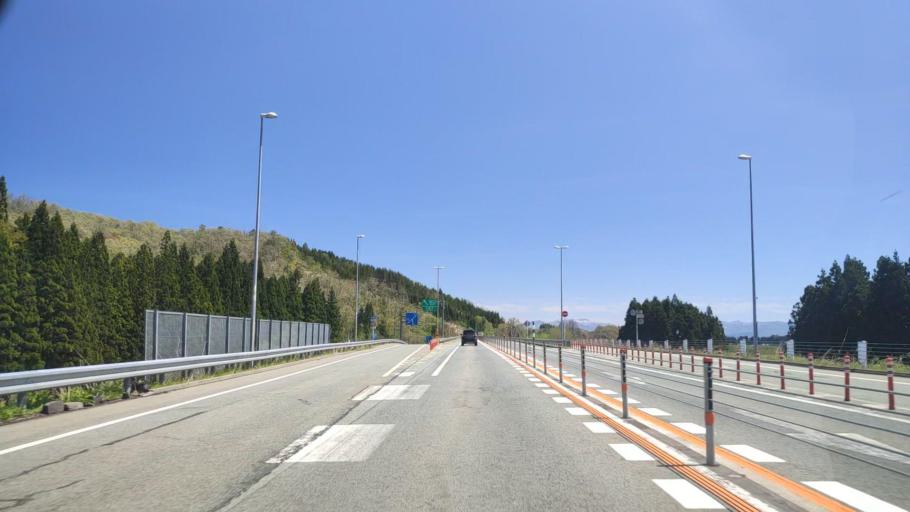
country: JP
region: Yamagata
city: Shinjo
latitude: 38.6748
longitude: 140.3244
